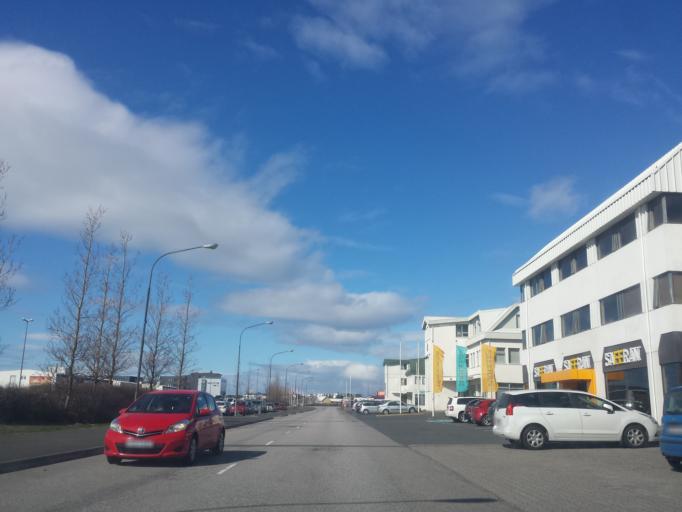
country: IS
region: Capital Region
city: Hafnarfjoerdur
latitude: 64.0794
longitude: -21.9405
